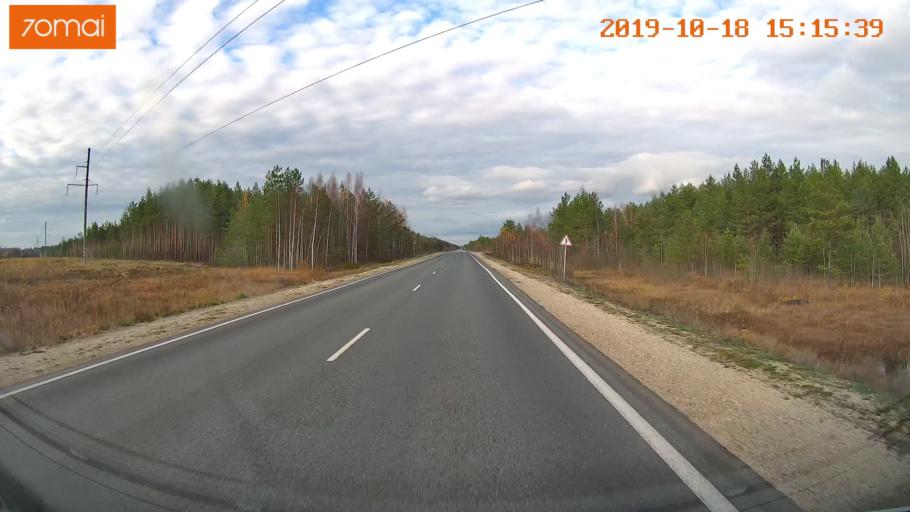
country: RU
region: Vladimir
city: Gus'-Khrustal'nyy
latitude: 55.6228
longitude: 40.7230
